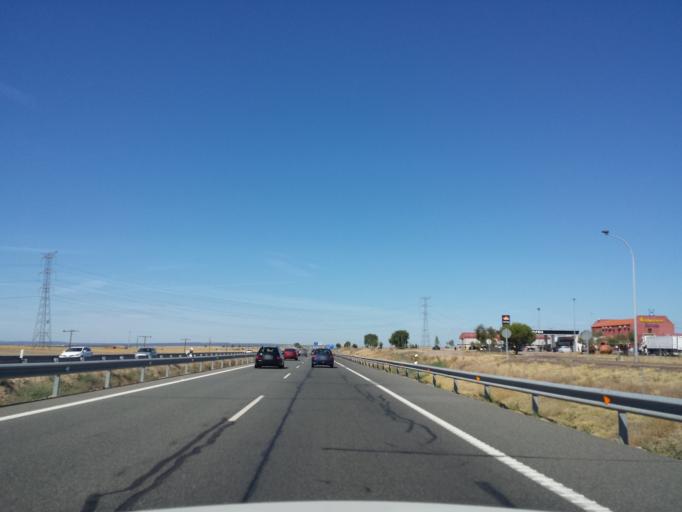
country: ES
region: Castille-La Mancha
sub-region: Province of Toledo
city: Caleruela
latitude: 39.8951
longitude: -5.3306
